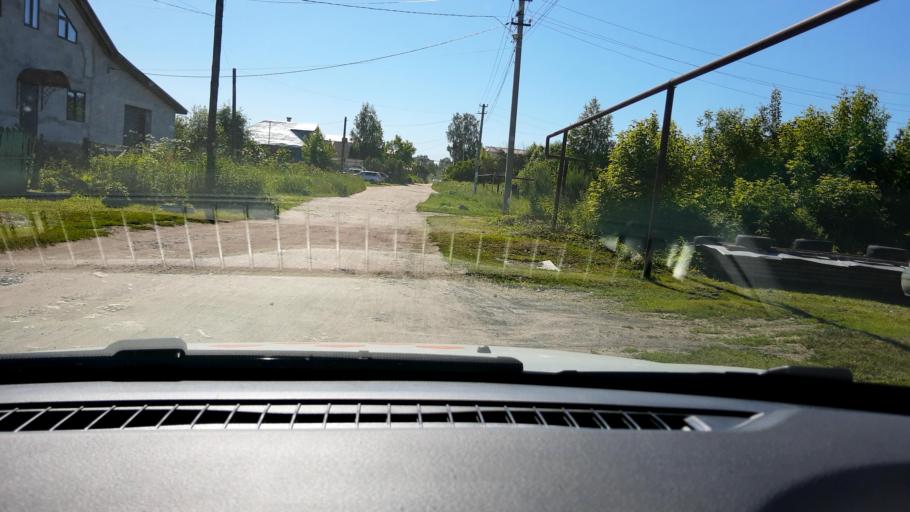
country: RU
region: Nizjnij Novgorod
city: Bor
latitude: 56.3942
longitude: 44.0462
